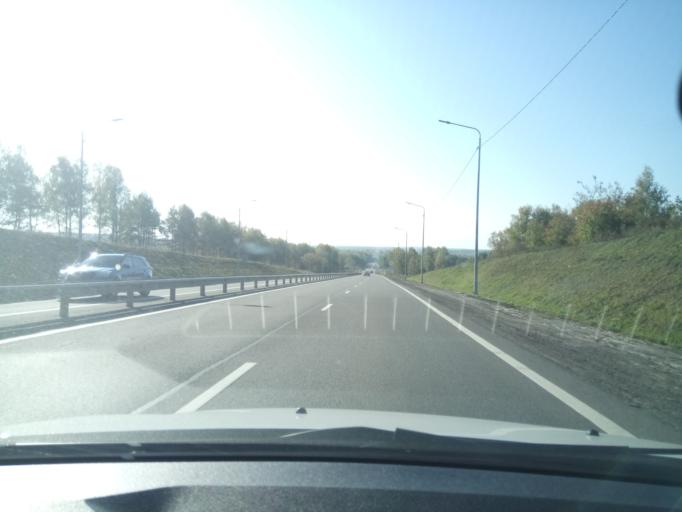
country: RU
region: Nizjnij Novgorod
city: Dal'neye Konstantinovo
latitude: 55.9930
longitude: 43.9690
